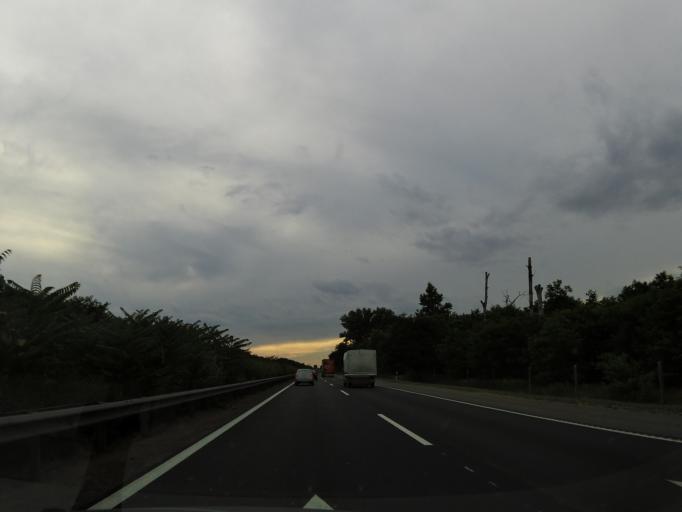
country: HU
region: Pest
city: Felsopakony
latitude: 47.3215
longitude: 19.2502
